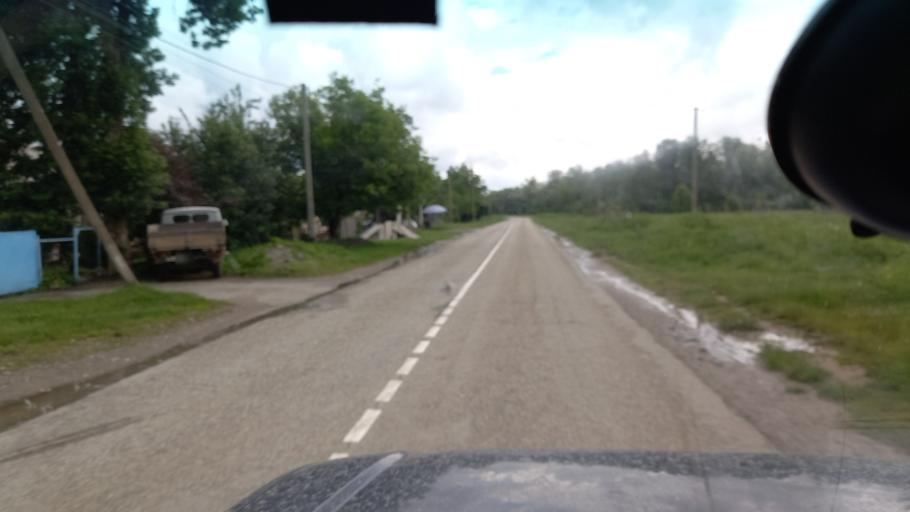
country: RU
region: Krasnodarskiy
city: Psebay
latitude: 44.0540
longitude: 40.7686
